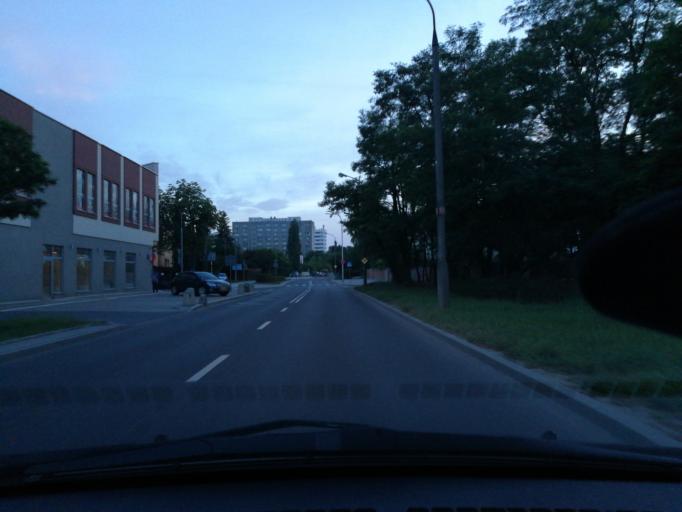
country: PL
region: Masovian Voivodeship
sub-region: Warszawa
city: Wilanow
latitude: 52.1778
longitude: 21.0686
